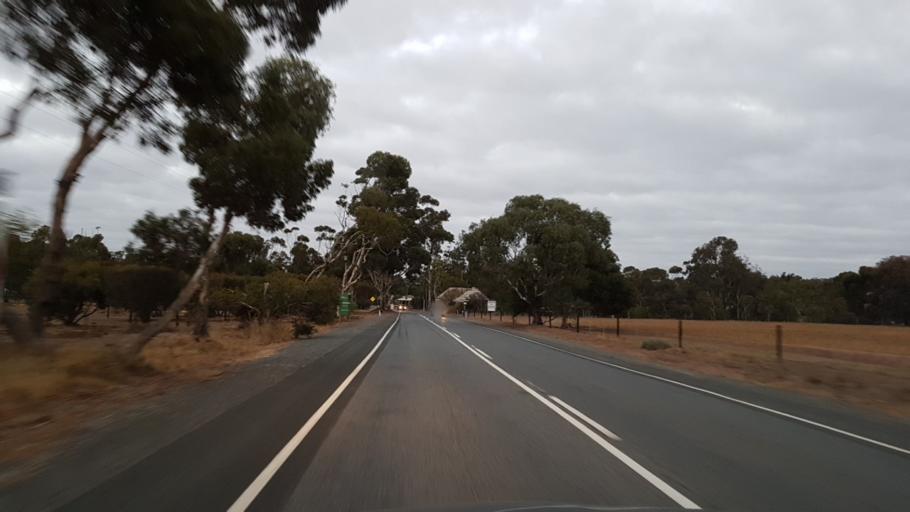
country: AU
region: South Australia
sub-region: Mount Barker
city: Callington
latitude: -35.0665
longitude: 139.0126
